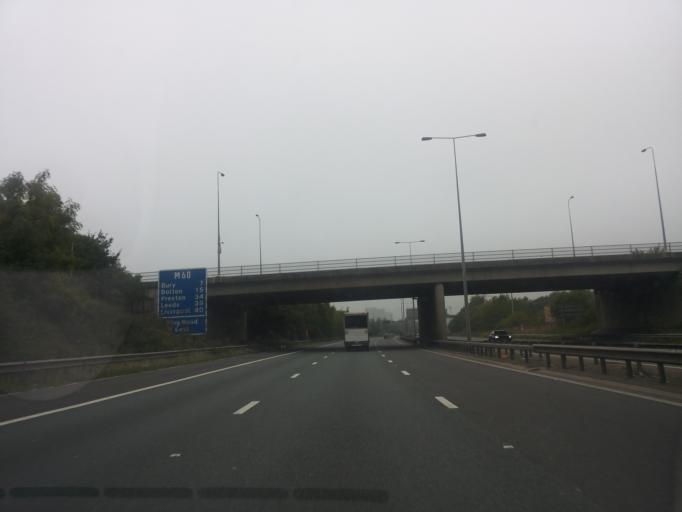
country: GB
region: England
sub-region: Manchester
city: Failsworth
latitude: 53.5275
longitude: -2.1749
